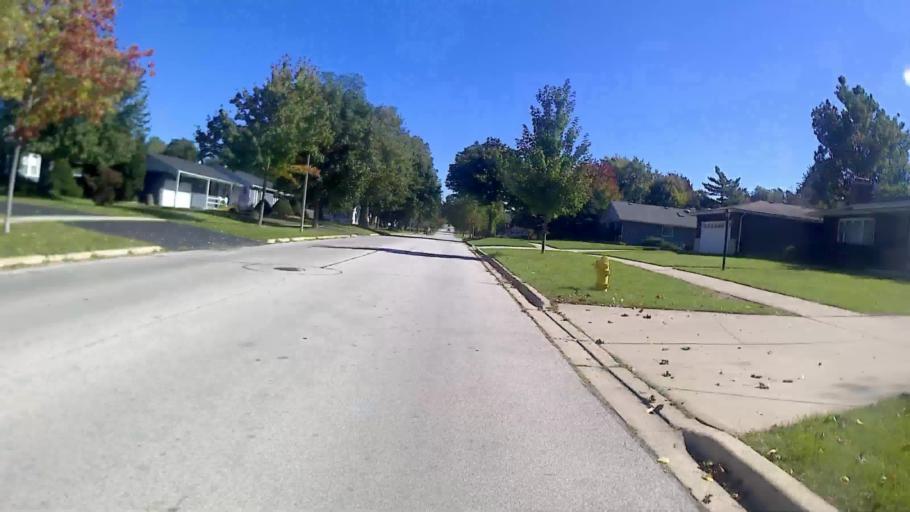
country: US
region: Illinois
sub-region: DuPage County
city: Lombard
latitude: 41.9005
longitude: -88.0156
